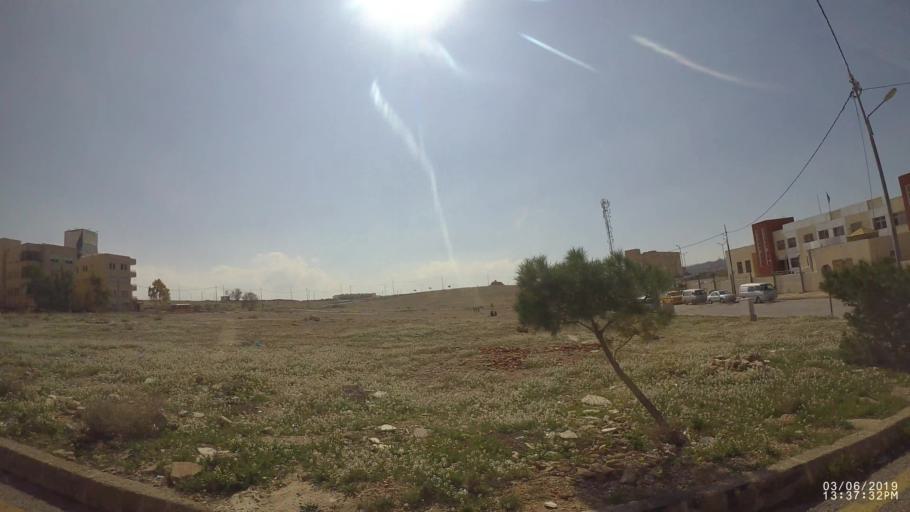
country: JO
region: Zarqa
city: Zarqa
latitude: 32.0755
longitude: 36.1114
